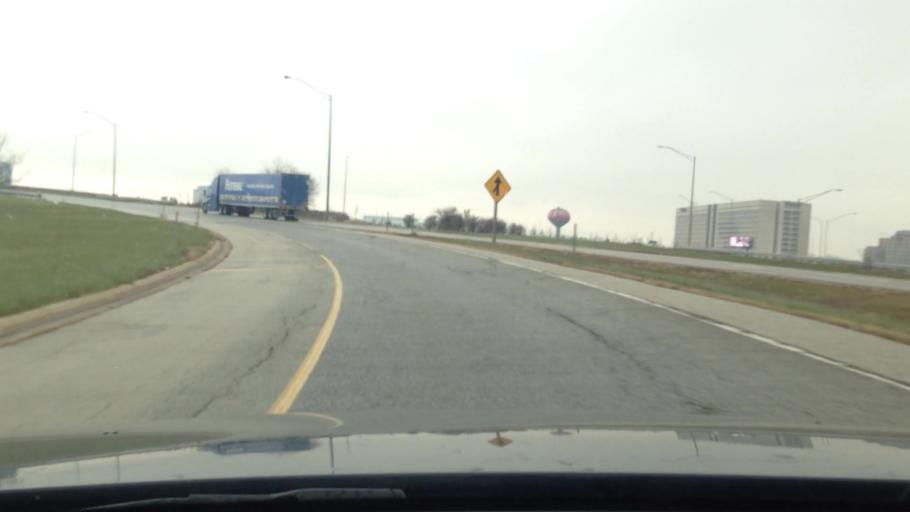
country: US
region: Illinois
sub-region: Cook County
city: Rosemont
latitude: 41.9858
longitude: -87.8673
